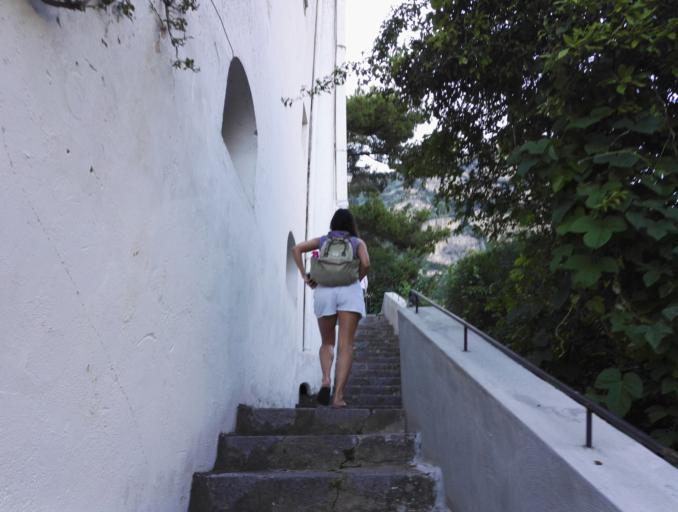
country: IT
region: Campania
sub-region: Provincia di Salerno
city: Positano
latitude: 40.6296
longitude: 14.4851
